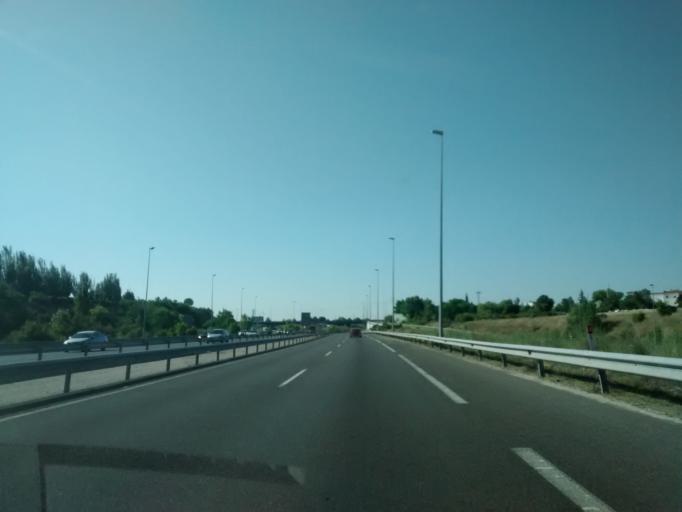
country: ES
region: Madrid
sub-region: Provincia de Madrid
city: Majadahonda
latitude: 40.4594
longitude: -3.8816
